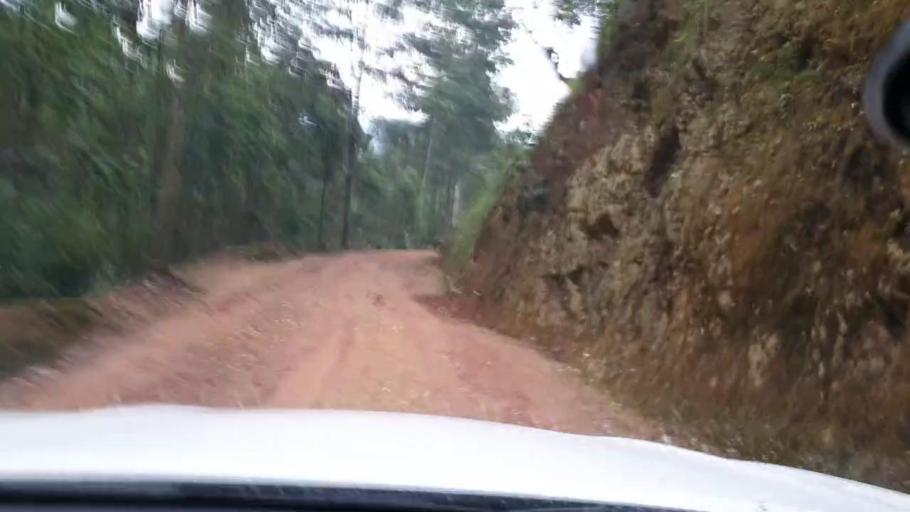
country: RW
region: Western Province
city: Cyangugu
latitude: -2.4084
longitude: 29.2048
